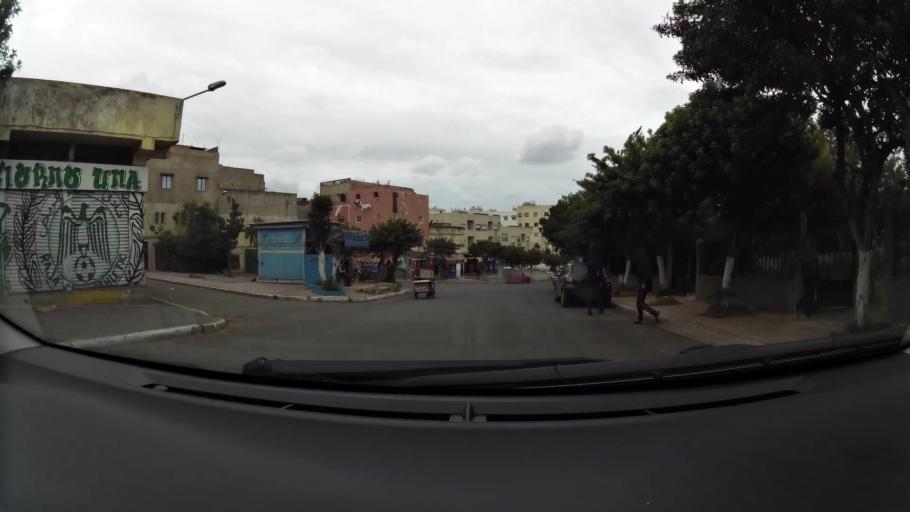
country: MA
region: Grand Casablanca
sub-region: Mediouna
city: Tit Mellil
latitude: 33.5674
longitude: -7.5464
